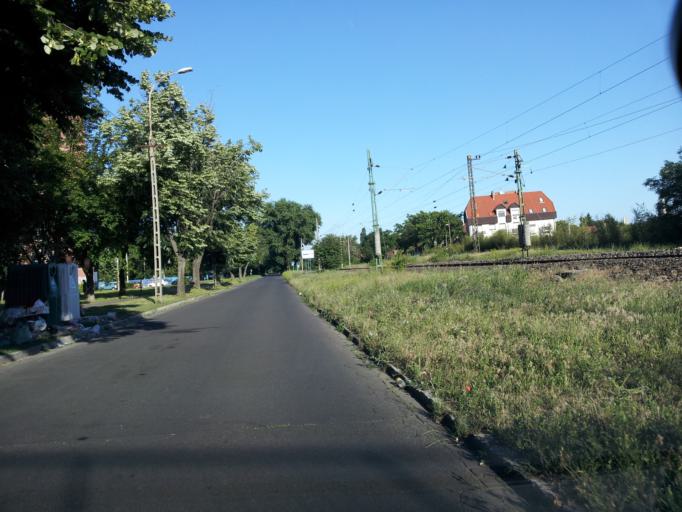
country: HU
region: Budapest
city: Budapest XIV. keruelet
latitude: 47.5314
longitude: 19.1279
